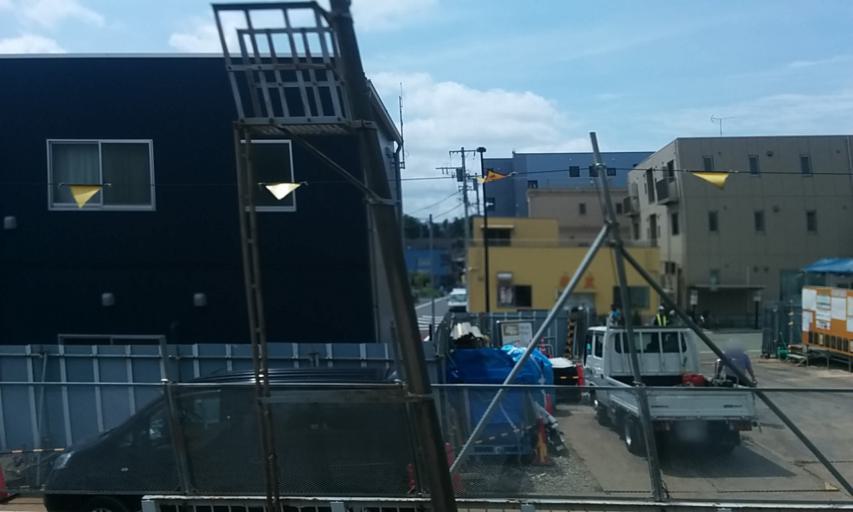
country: JP
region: Chiba
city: Yotsukaido
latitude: 35.7120
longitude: 140.1076
